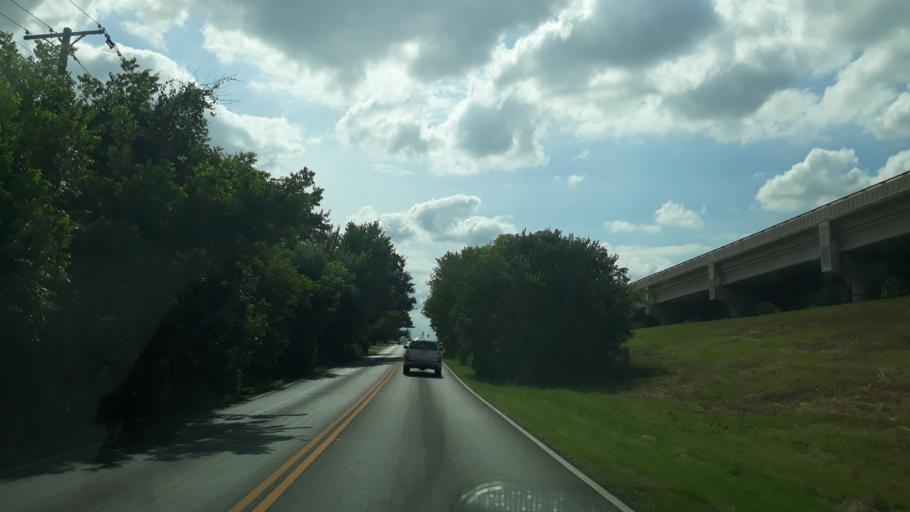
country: US
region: Texas
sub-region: Dallas County
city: Irving
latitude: 32.8156
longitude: -96.9960
